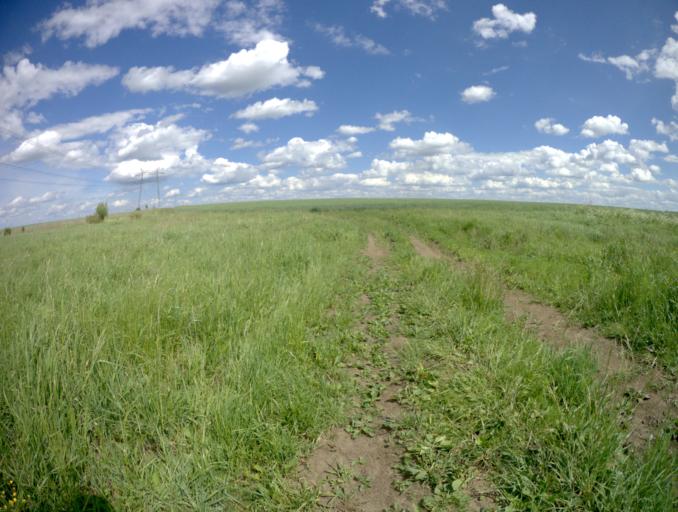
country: RU
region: Vladimir
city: Suzdal'
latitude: 56.4376
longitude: 40.3665
